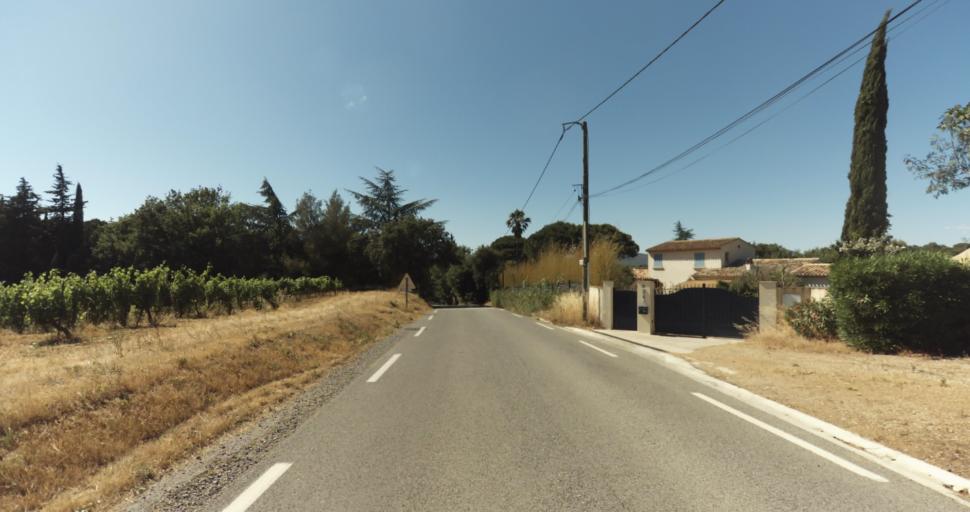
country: FR
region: Provence-Alpes-Cote d'Azur
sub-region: Departement du Var
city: Gassin
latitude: 43.2335
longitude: 6.5777
